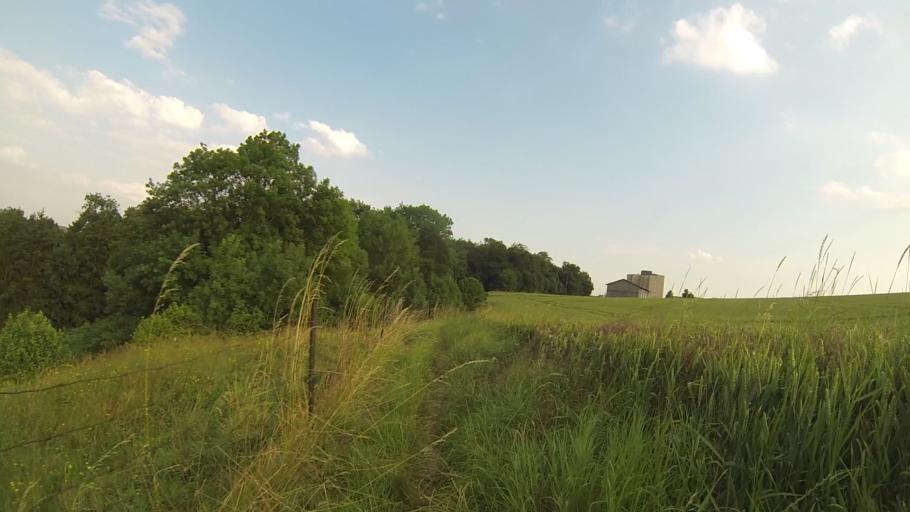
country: DE
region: Baden-Wuerttemberg
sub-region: Tuebingen Region
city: Dornstadt
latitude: 48.4284
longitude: 9.8854
